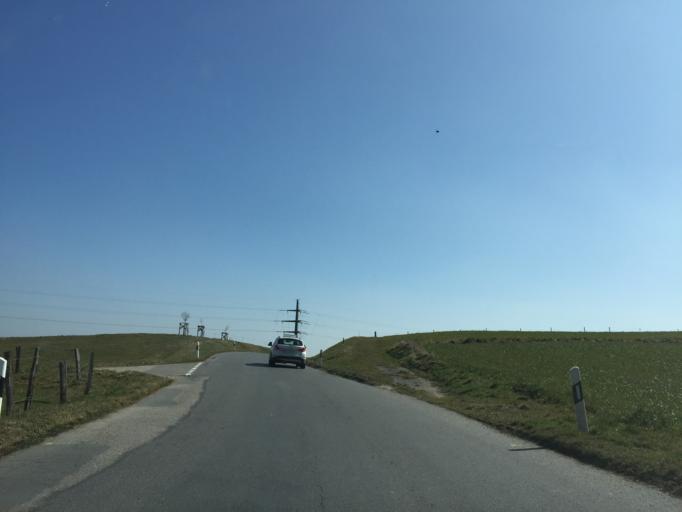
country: CH
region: Vaud
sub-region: Morges District
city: Cossonay
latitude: 46.6318
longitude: 6.4971
